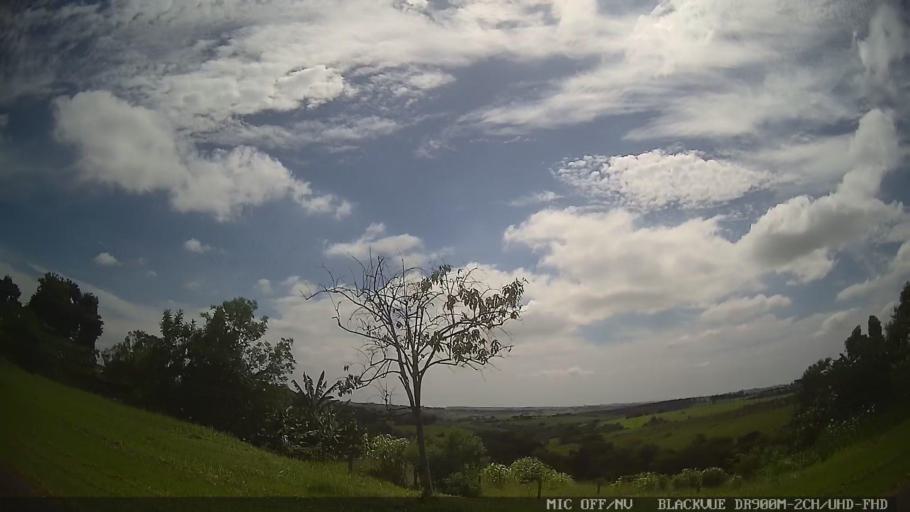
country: BR
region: Sao Paulo
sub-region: Tiete
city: Tiete
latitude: -23.0927
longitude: -47.7783
